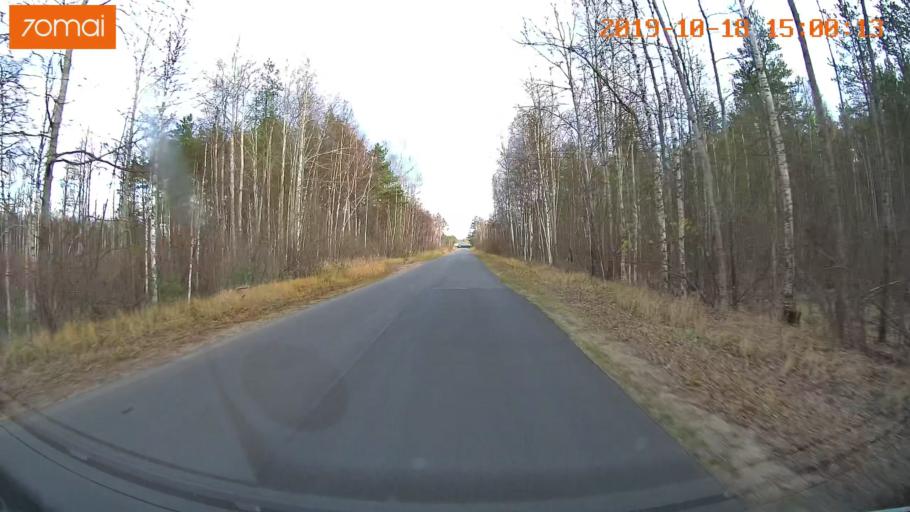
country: RU
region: Vladimir
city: Kurlovo
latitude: 55.4983
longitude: 40.5804
